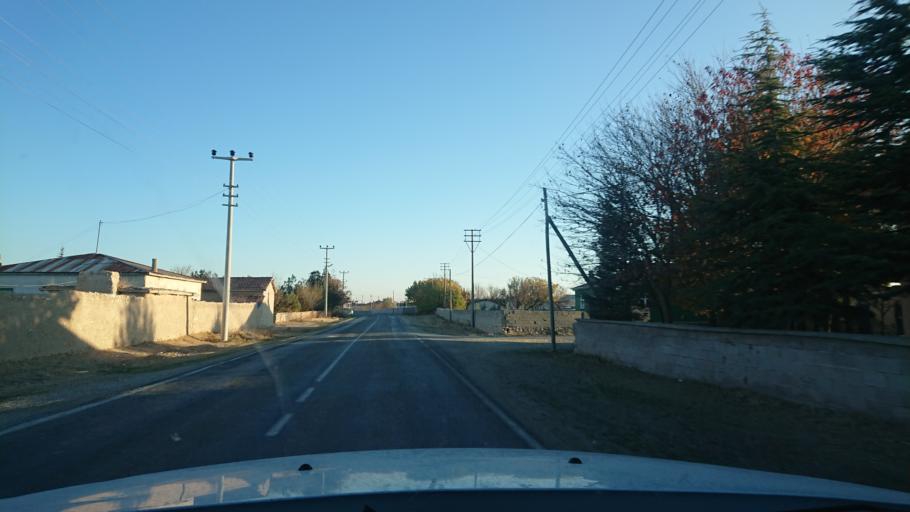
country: TR
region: Aksaray
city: Eskil
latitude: 38.4244
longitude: 33.2824
